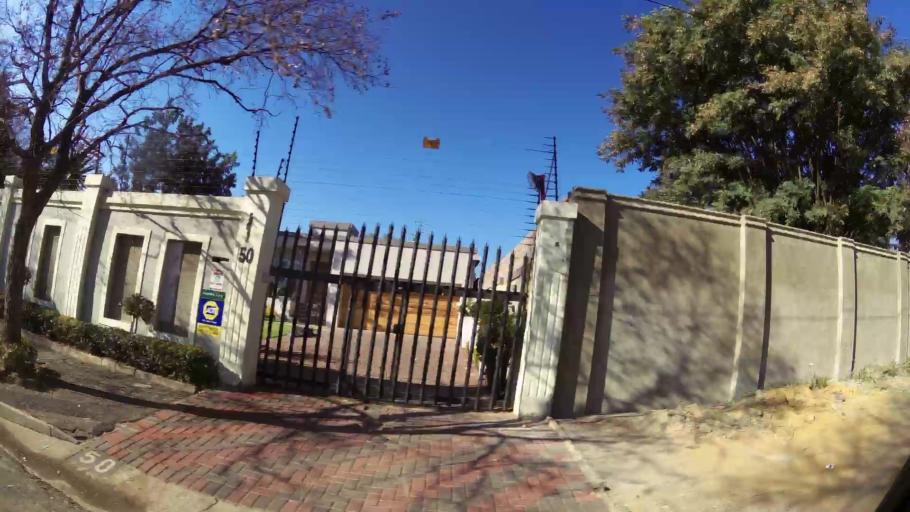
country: ZA
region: Gauteng
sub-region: City of Johannesburg Metropolitan Municipality
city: Johannesburg
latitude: -26.1862
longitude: 28.1088
